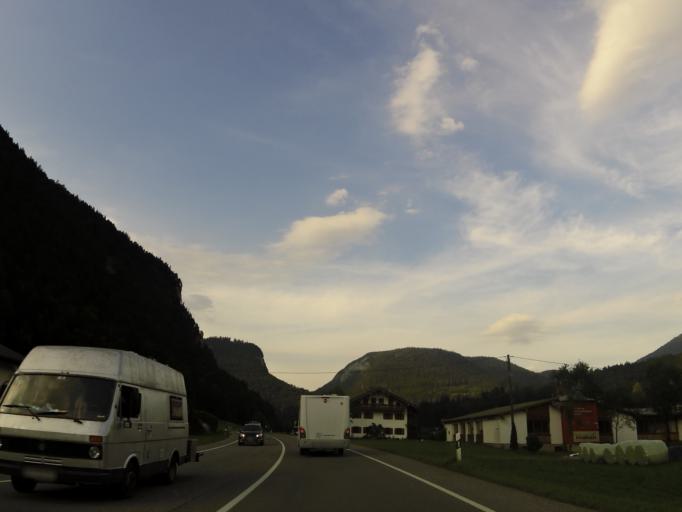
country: DE
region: Bavaria
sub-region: Upper Bavaria
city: Berchtesgaden
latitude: 47.6454
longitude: 13.0292
